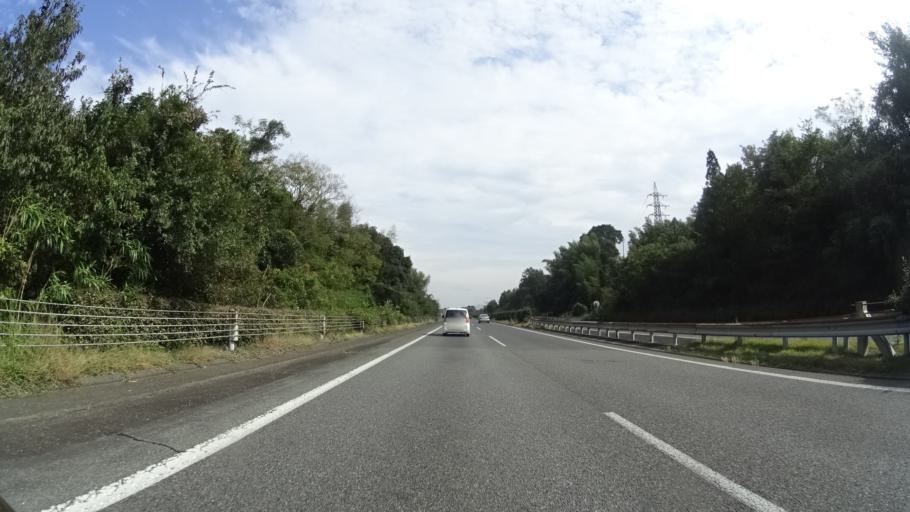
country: JP
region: Kumamoto
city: Yatsushiro
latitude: 32.5400
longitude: 130.6766
